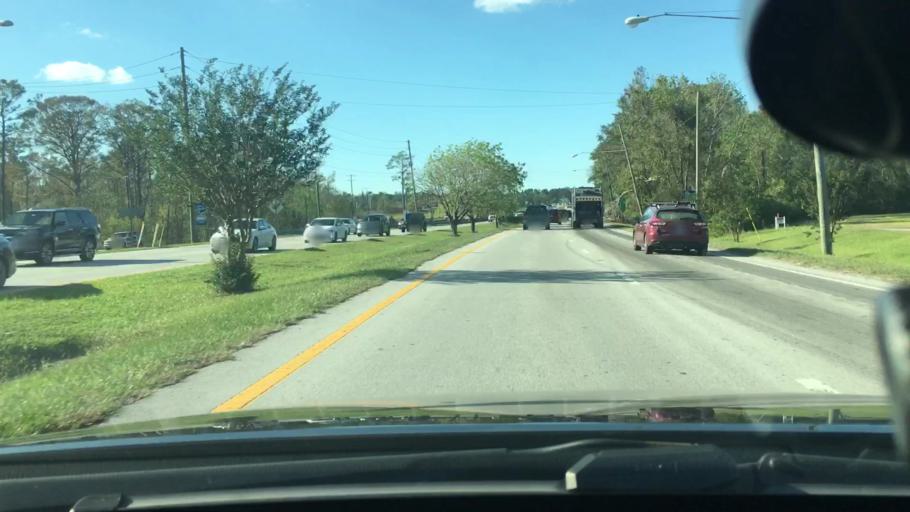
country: US
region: North Carolina
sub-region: Craven County
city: Havelock
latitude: 34.8901
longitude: -76.9214
